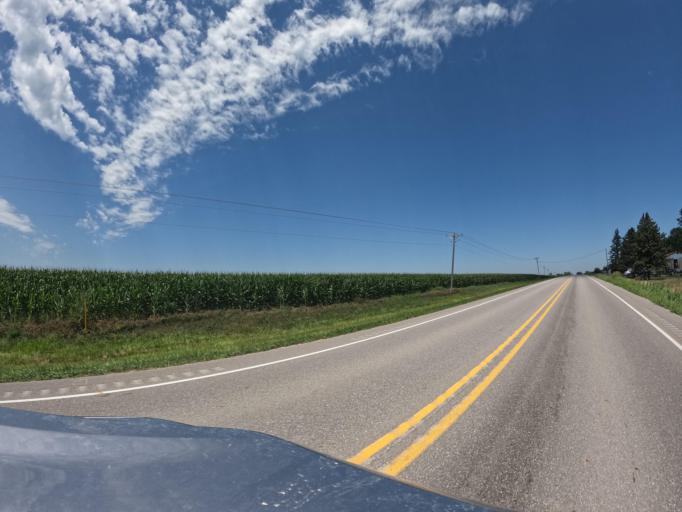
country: US
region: Iowa
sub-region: Keokuk County
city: Sigourney
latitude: 41.4147
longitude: -92.3548
